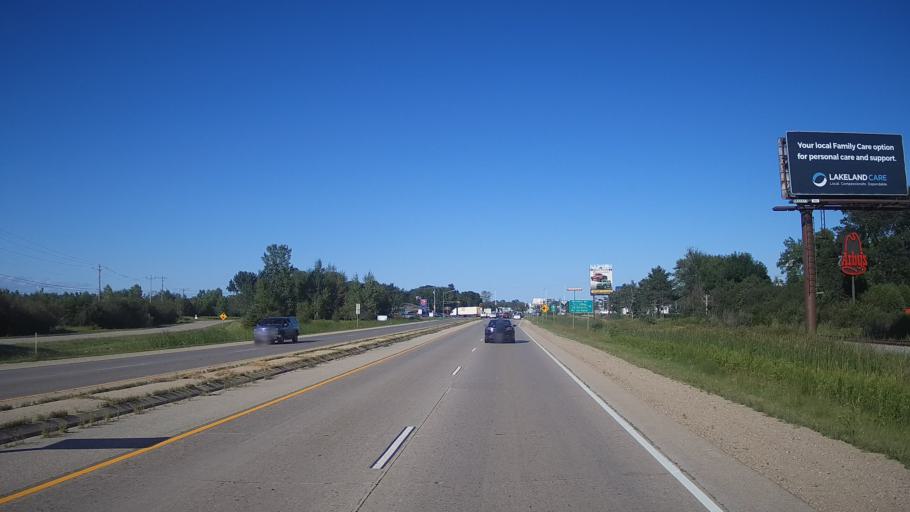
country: US
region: Wisconsin
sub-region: Marinette County
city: Marinette
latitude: 45.0809
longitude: -87.6634
